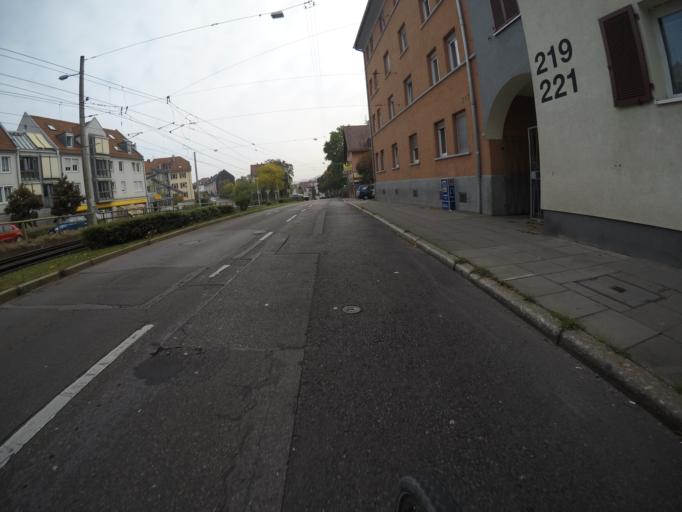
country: DE
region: Baden-Wuerttemberg
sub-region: Regierungsbezirk Stuttgart
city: Stuttgart
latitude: 48.7568
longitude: 9.1452
